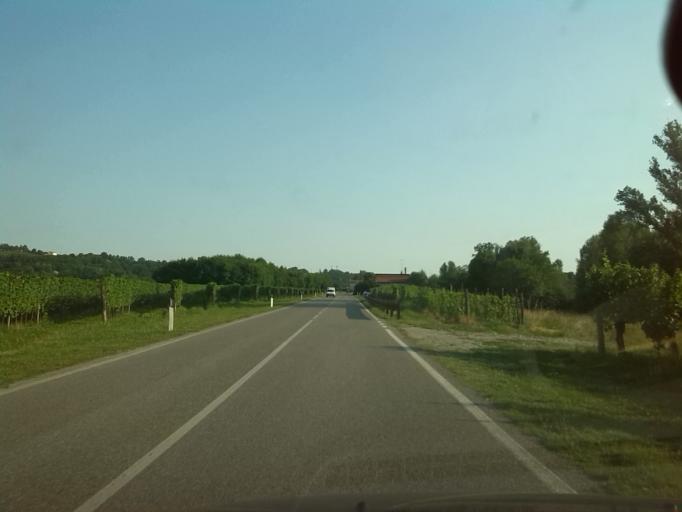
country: IT
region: Friuli Venezia Giulia
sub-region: Provincia di Gorizia
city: Dolegna del Collio
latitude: 46.0282
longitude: 13.4772
